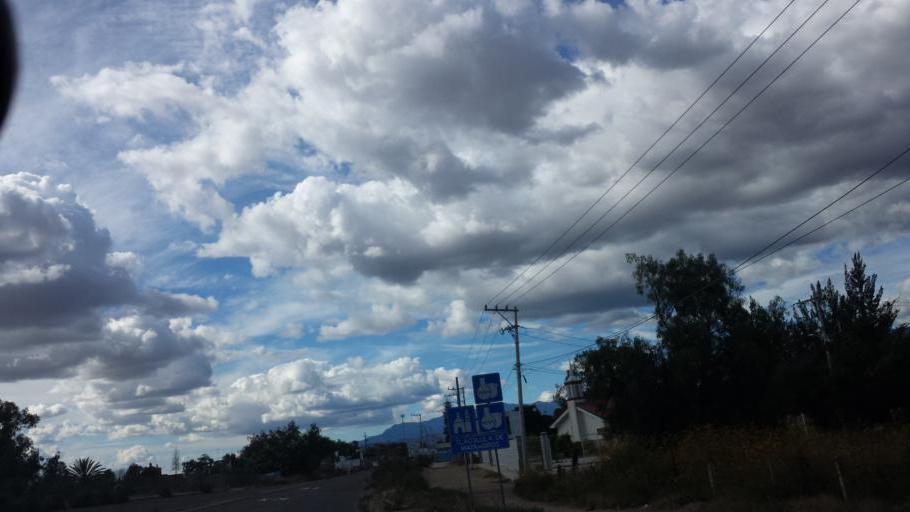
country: MX
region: Oaxaca
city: Tlacolula de Matamoros
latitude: 16.9520
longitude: -96.4676
